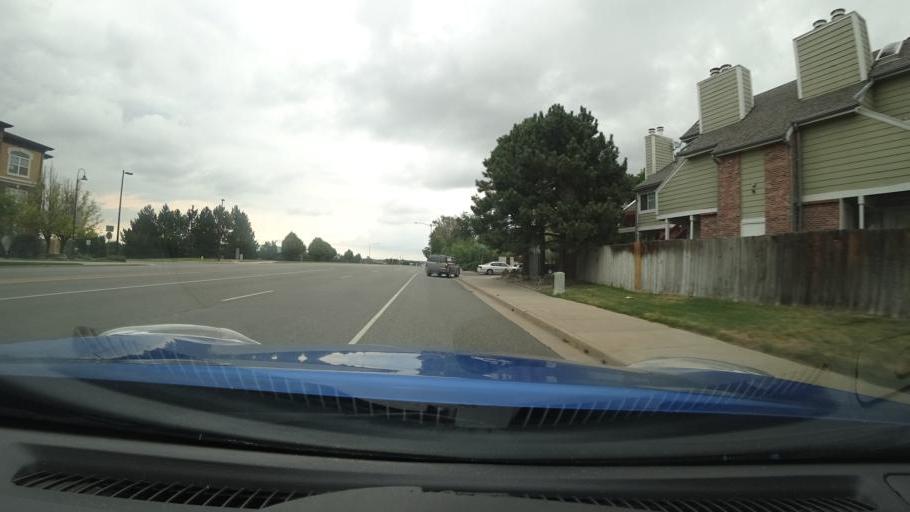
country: US
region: Colorado
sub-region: Adams County
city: Aurora
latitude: 39.7006
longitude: -104.8191
